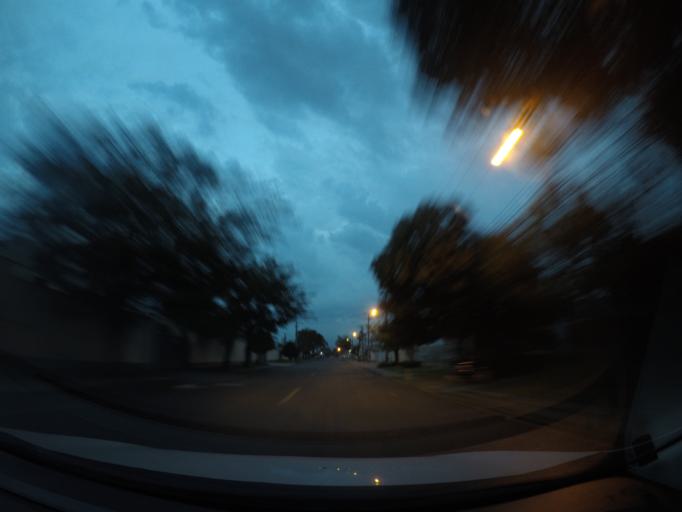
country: BR
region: Parana
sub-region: Sao Jose Dos Pinhais
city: Sao Jose dos Pinhais
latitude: -25.5108
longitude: -49.2275
